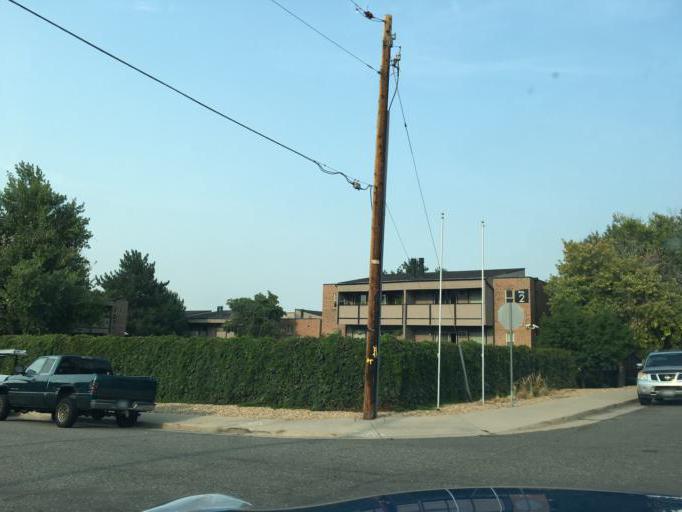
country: US
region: Colorado
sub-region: Arapahoe County
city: Glendale
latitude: 39.6948
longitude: -104.9364
